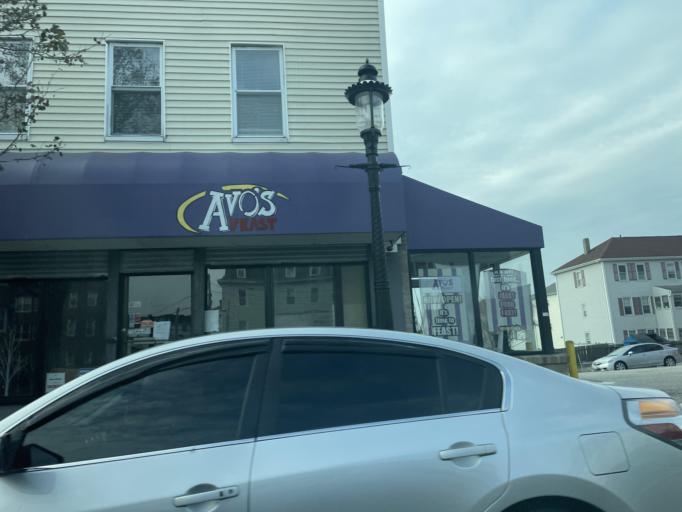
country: US
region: Massachusetts
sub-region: Bristol County
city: Fall River
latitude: 41.6887
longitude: -71.1321
